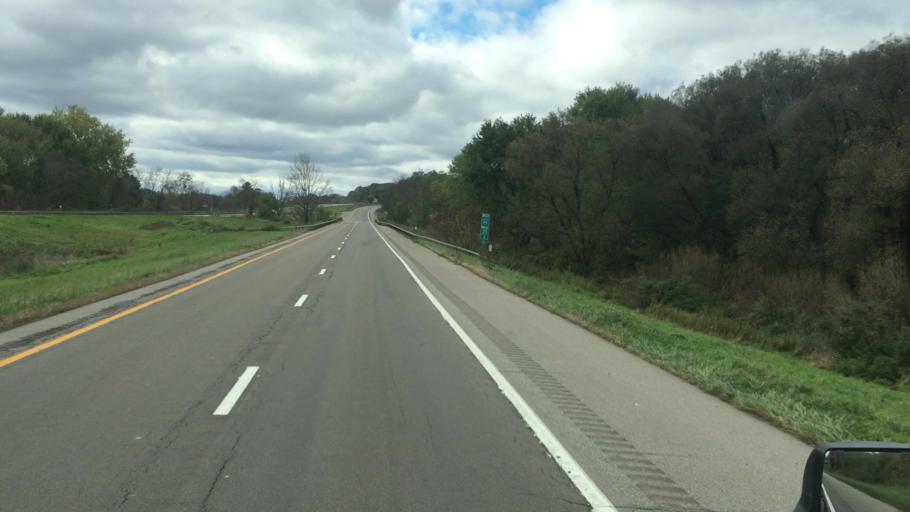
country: US
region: New York
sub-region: Chautauqua County
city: Falconer
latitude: 42.1418
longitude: -79.1013
